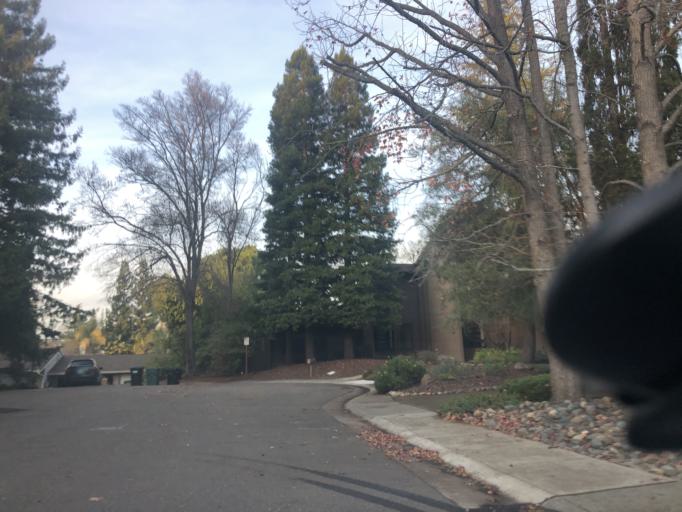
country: US
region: California
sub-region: Sacramento County
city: Gold River
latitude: 38.6431
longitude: -121.2305
